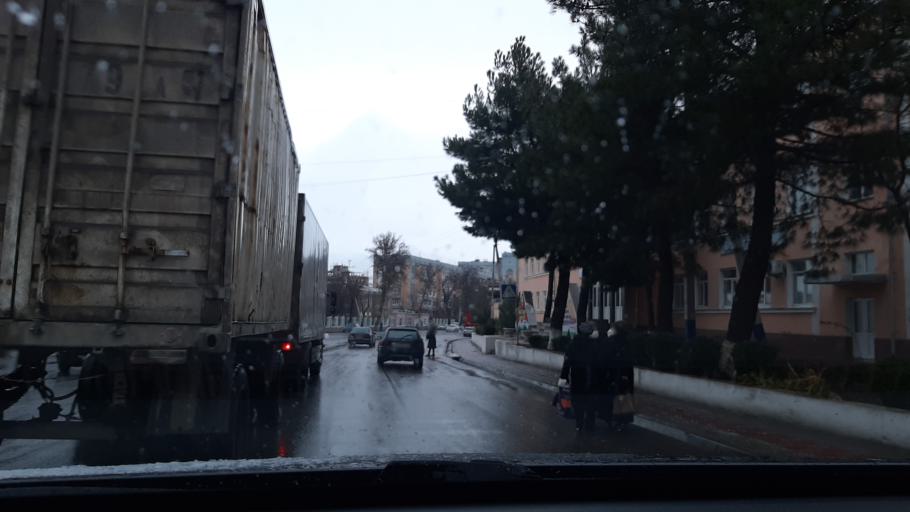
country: TJ
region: Viloyati Sughd
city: Khujand
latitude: 40.2744
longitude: 69.6414
